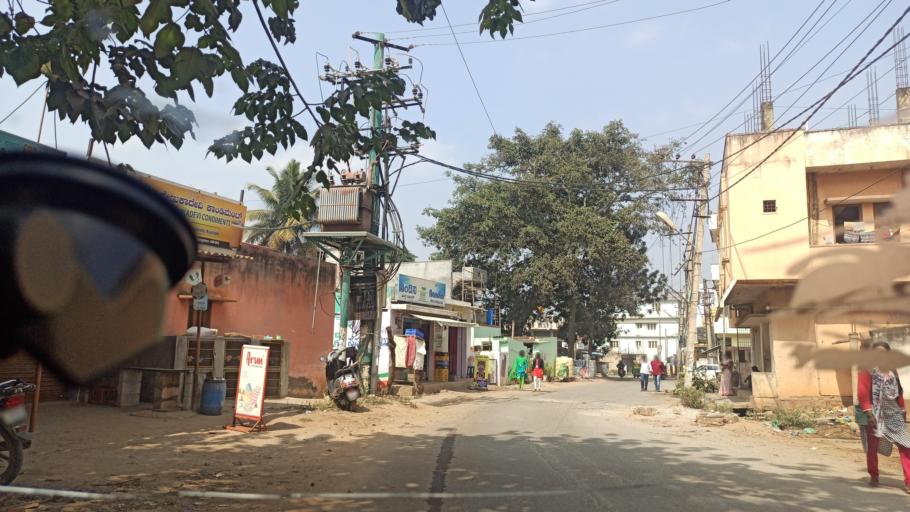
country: IN
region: Karnataka
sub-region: Bangalore Urban
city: Yelahanka
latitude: 13.1027
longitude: 77.6166
